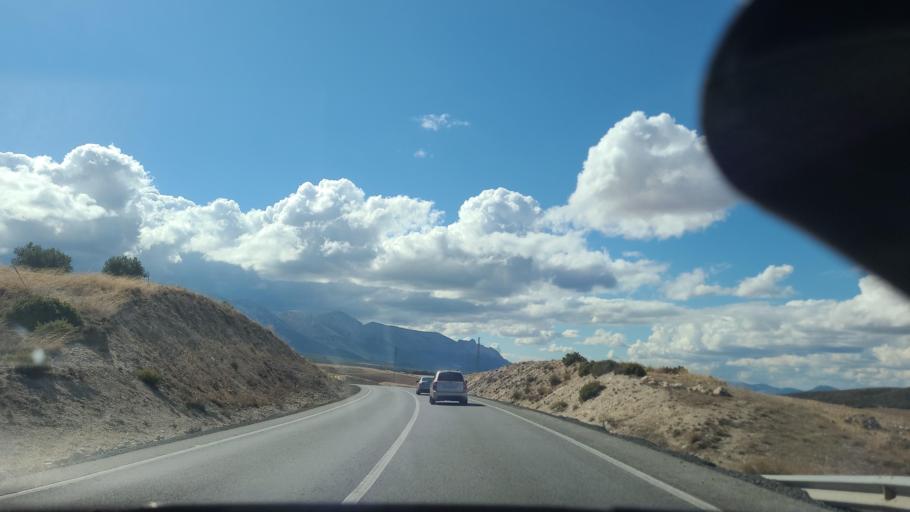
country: ES
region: Andalusia
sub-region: Provincia de Granada
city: Pinar
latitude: 37.4103
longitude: -3.3691
